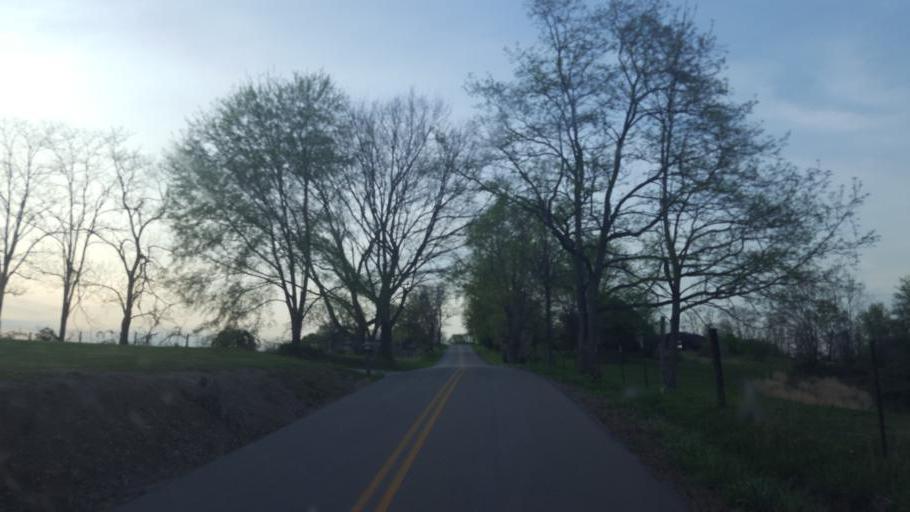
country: US
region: Kentucky
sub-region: Metcalfe County
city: Edmonton
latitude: 37.0622
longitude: -85.7060
